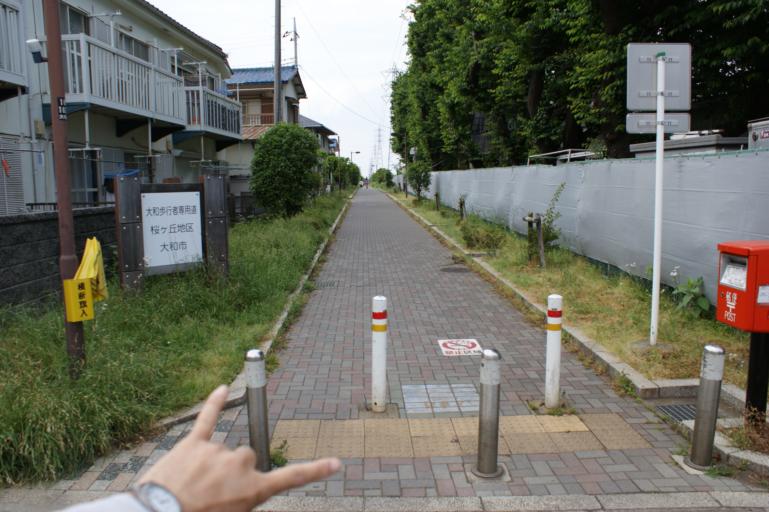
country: JP
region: Kanagawa
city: Minami-rinkan
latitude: 35.4524
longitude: 139.4679
